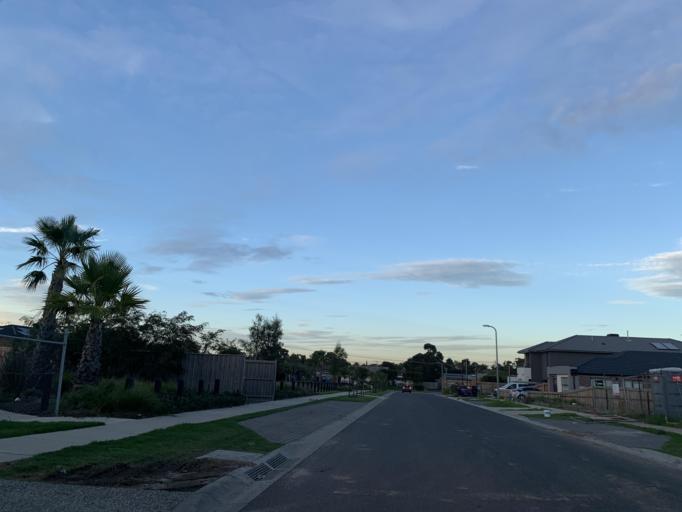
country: AU
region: Victoria
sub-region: Casey
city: Cranbourne North
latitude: -38.0737
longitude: 145.2768
